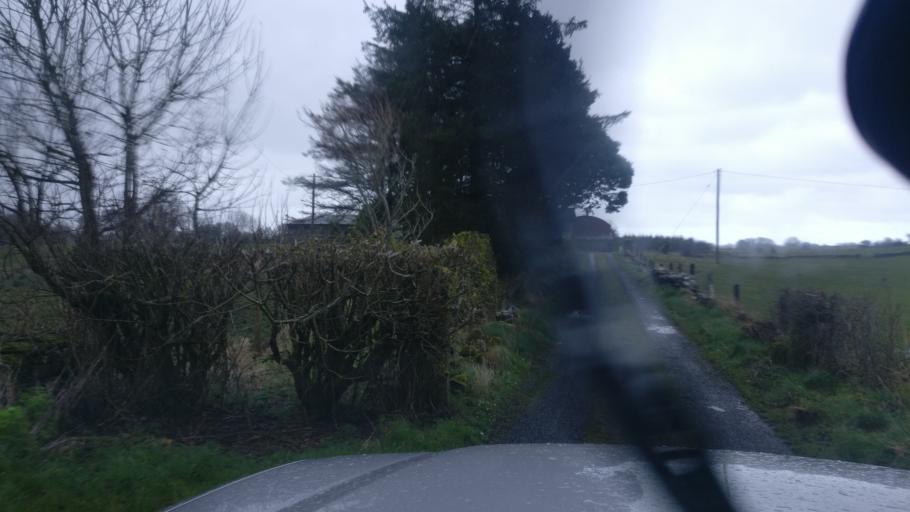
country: IE
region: Connaught
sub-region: County Galway
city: Loughrea
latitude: 53.2434
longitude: -8.4234
